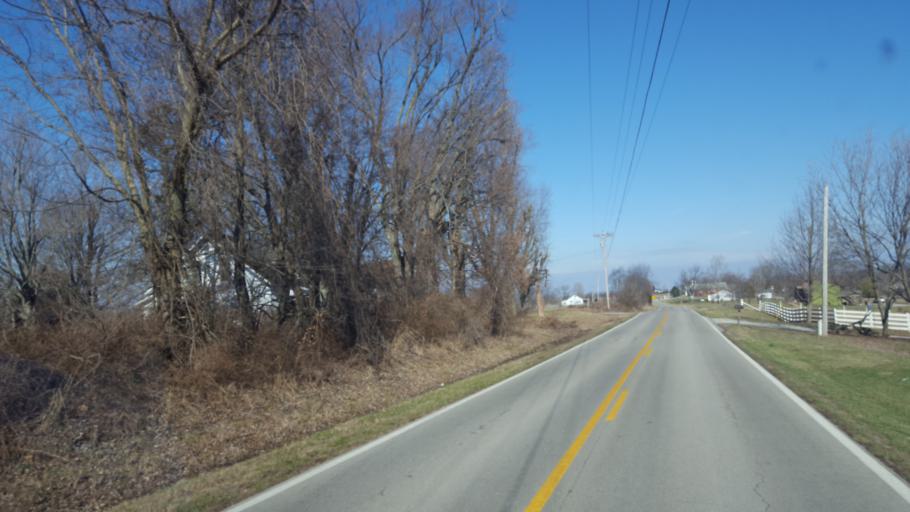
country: US
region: Kentucky
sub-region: Shelby County
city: Shelbyville
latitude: 38.2113
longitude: -85.0656
